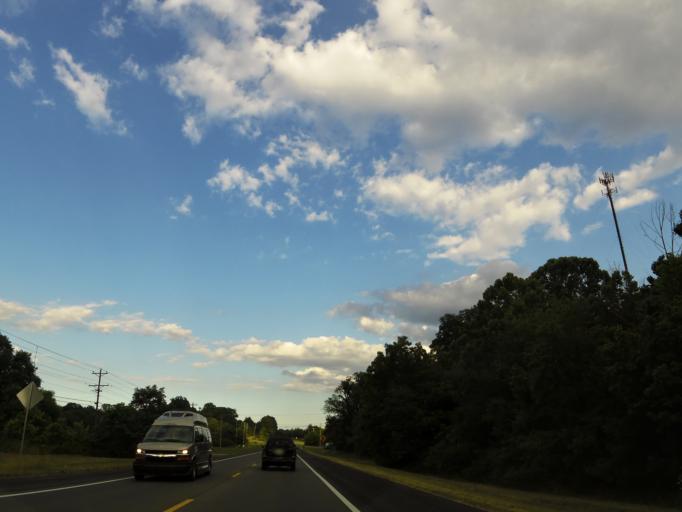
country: US
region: Tennessee
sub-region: Maury County
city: Columbia
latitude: 35.6348
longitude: -86.9578
